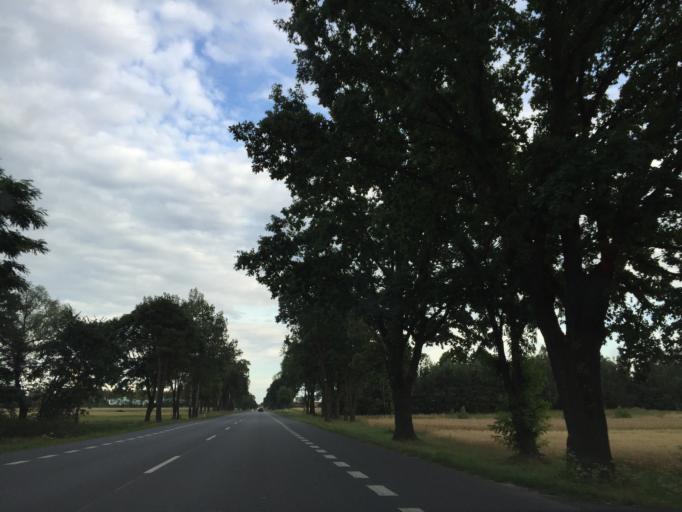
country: PL
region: Lublin Voivodeship
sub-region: Powiat lubartowski
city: Firlej
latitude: 51.5894
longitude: 22.4822
